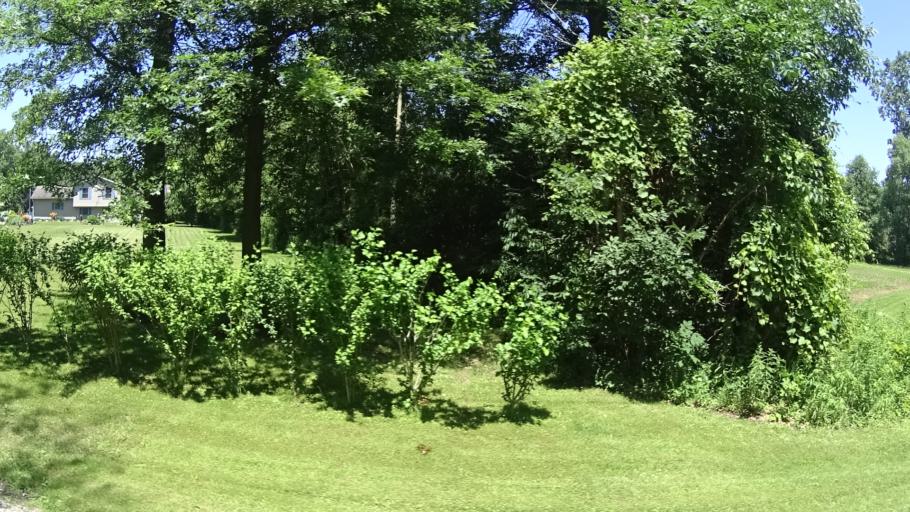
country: US
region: Ohio
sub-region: Lorain County
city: Vermilion
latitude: 41.3573
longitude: -82.4233
